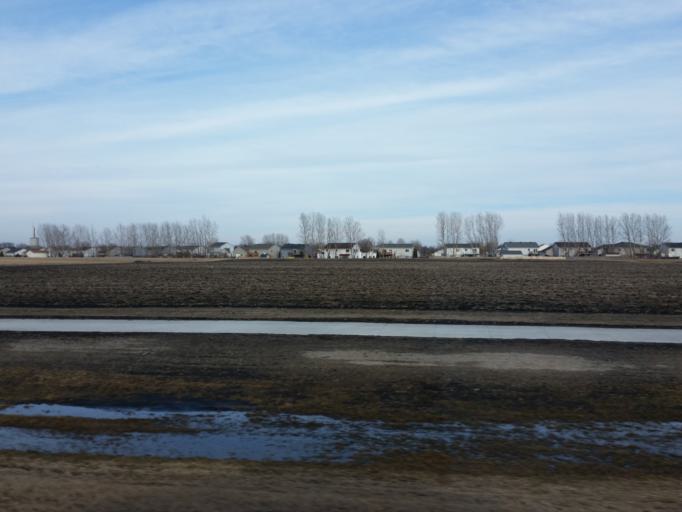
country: US
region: North Dakota
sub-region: Cass County
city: West Fargo
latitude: 46.8691
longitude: -96.9262
